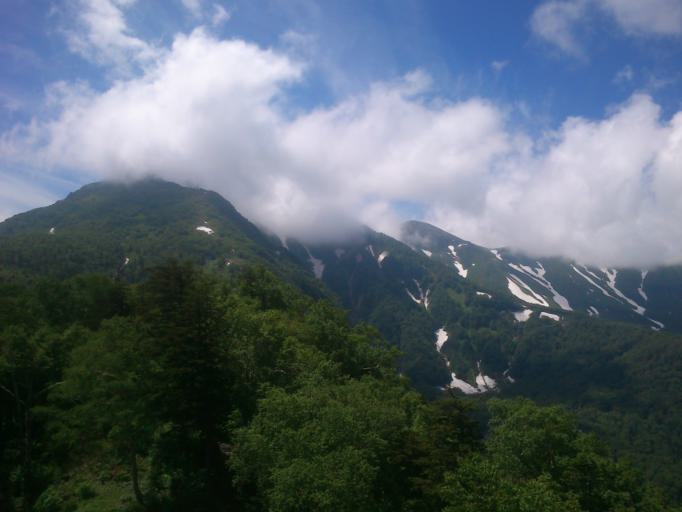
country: JP
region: Hokkaido
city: Kamikawa
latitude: 43.7250
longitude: 142.9462
